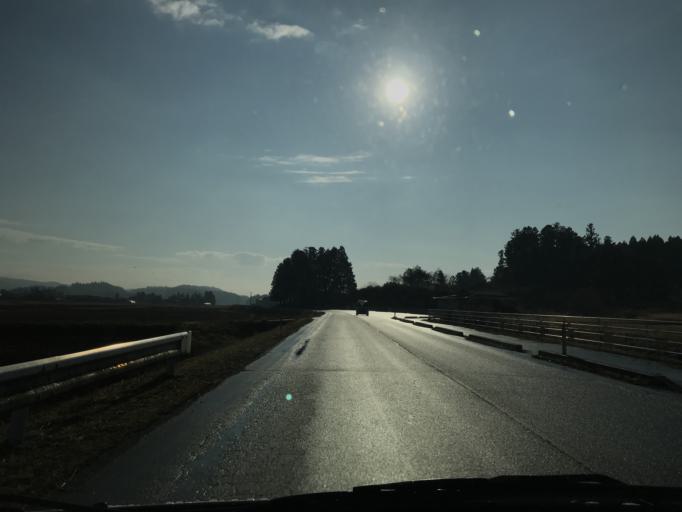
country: JP
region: Iwate
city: Ichinoseki
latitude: 38.7727
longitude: 141.1772
